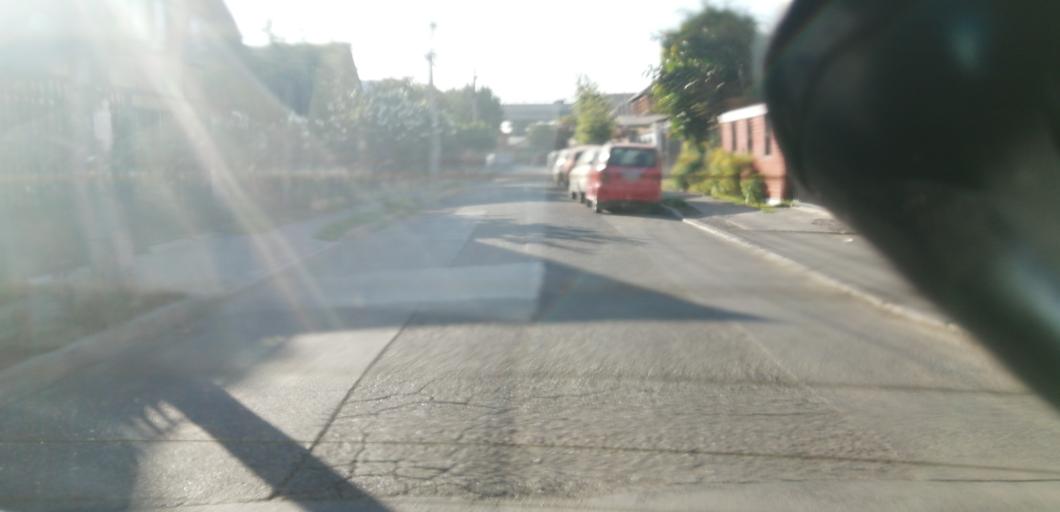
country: CL
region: Santiago Metropolitan
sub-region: Provincia de Santiago
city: Lo Prado
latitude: -33.4609
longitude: -70.7393
